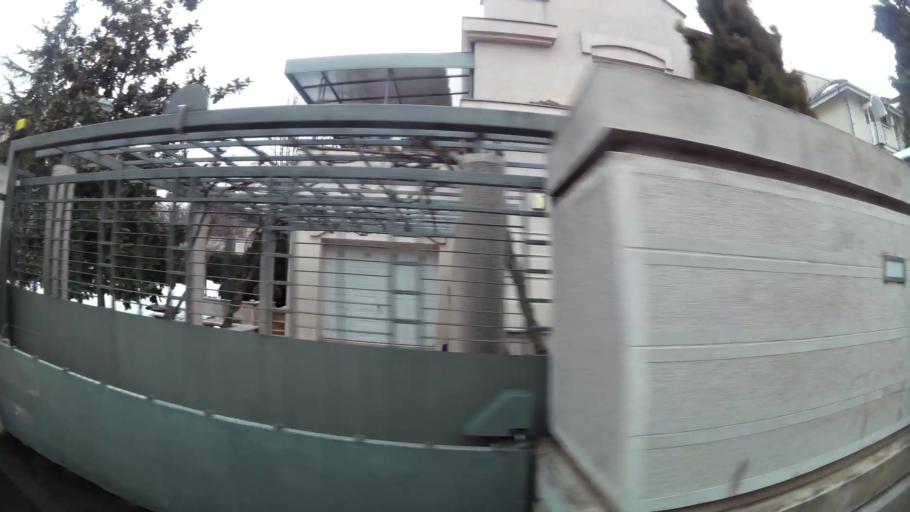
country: RS
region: Central Serbia
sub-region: Belgrade
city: Vozdovac
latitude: 44.7616
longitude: 20.5018
